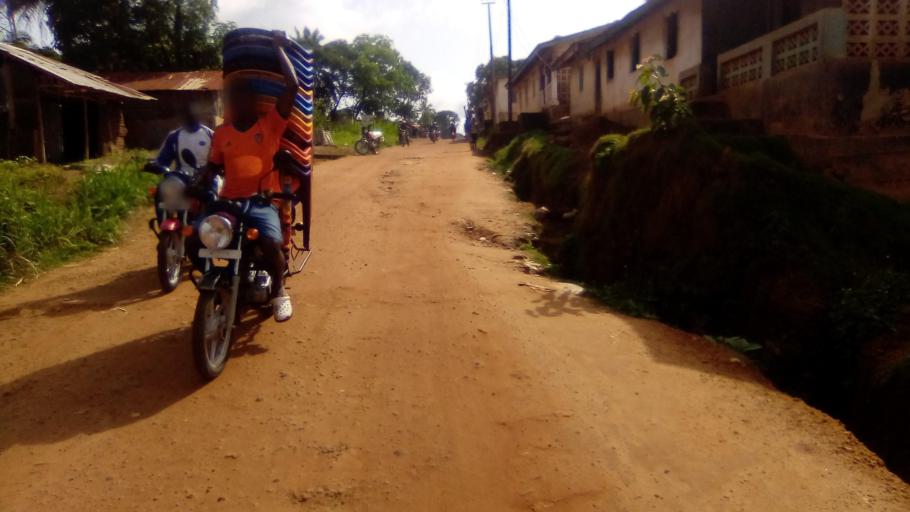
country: SL
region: Southern Province
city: Bo
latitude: 7.9765
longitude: -11.7289
